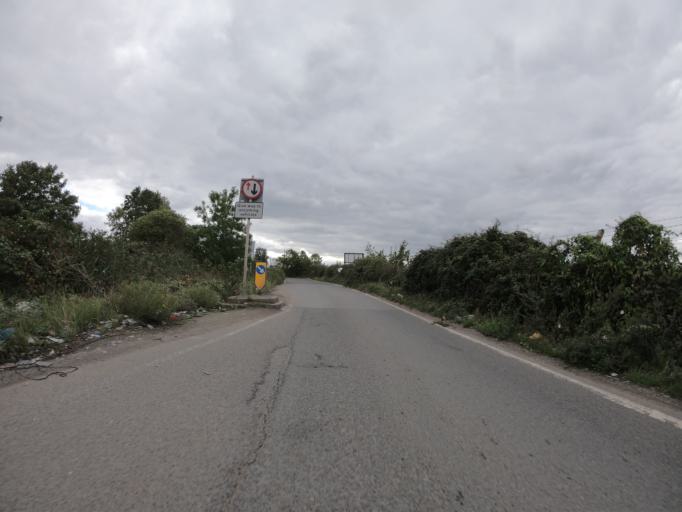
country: GB
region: England
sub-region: Essex
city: Purfleet
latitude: 51.4771
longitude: 0.2094
